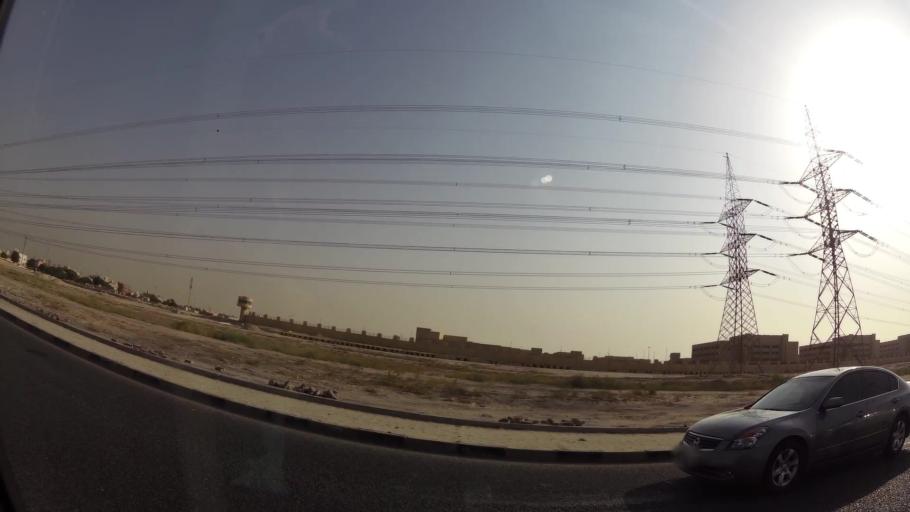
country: KW
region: Al Asimah
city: Ar Rabiyah
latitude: 29.2952
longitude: 47.8620
